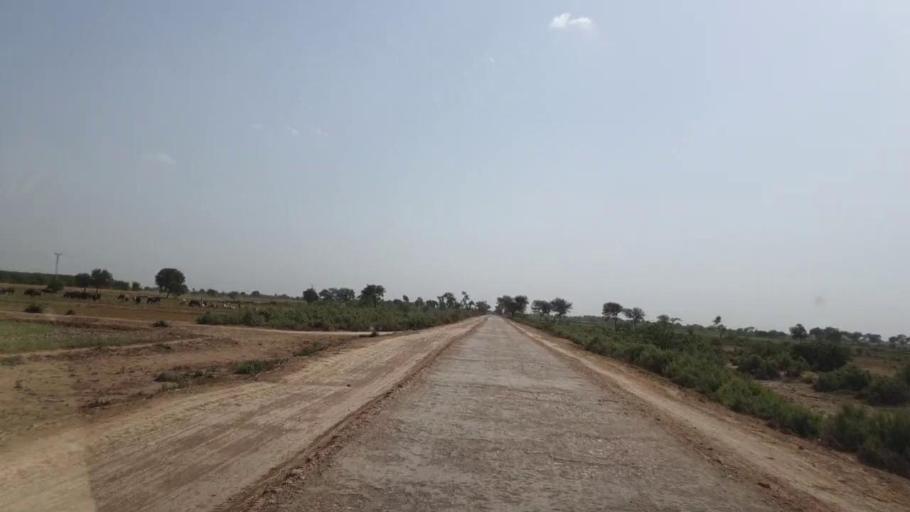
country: PK
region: Sindh
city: Rajo Khanani
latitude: 25.0201
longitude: 68.8730
